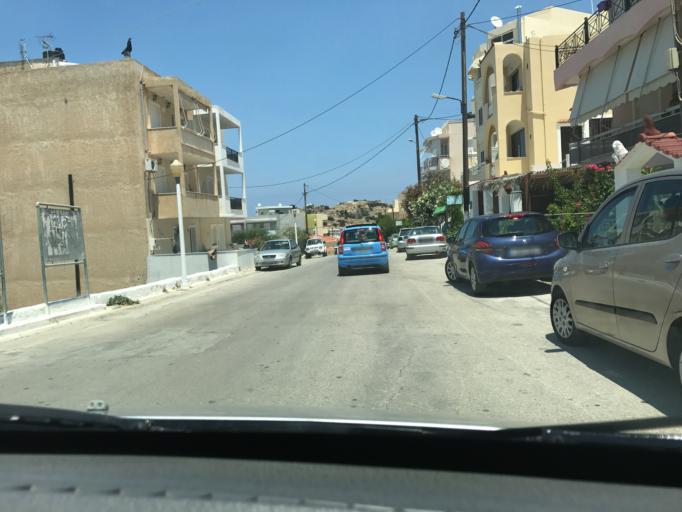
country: GR
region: South Aegean
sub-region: Nomos Dodekanisou
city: Karpathos
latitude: 35.5047
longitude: 27.2124
